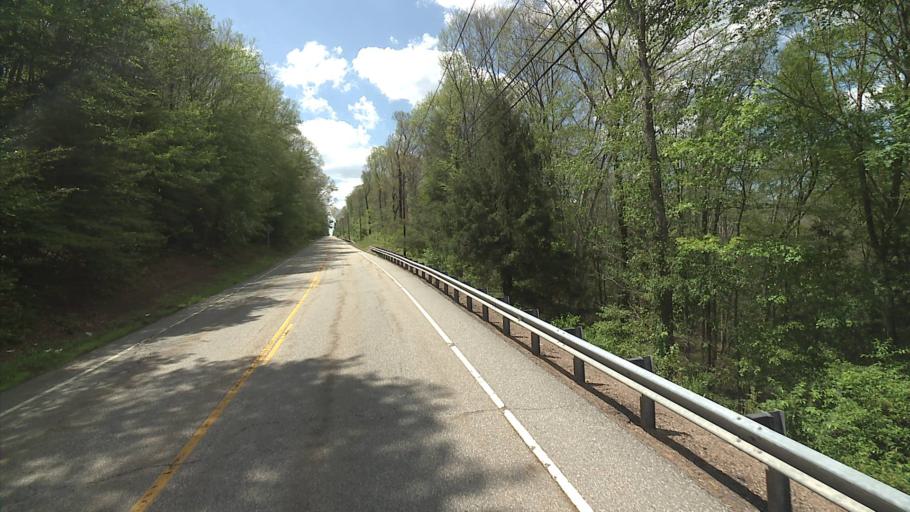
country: US
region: Connecticut
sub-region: Middlesex County
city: East Hampton
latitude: 41.5204
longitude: -72.5047
